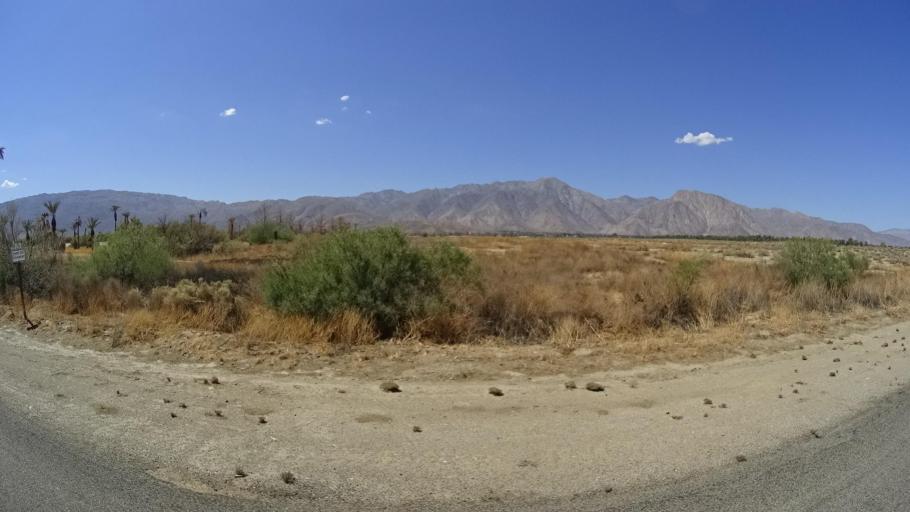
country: US
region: California
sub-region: San Diego County
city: Borrego Springs
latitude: 33.2500
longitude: -116.3478
